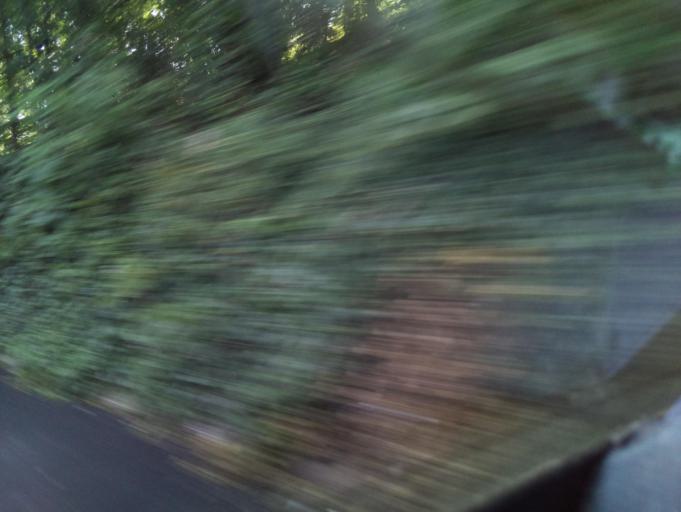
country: GB
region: Wales
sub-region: Caerphilly County Borough
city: Llanbradach
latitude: 51.5974
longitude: -3.2321
